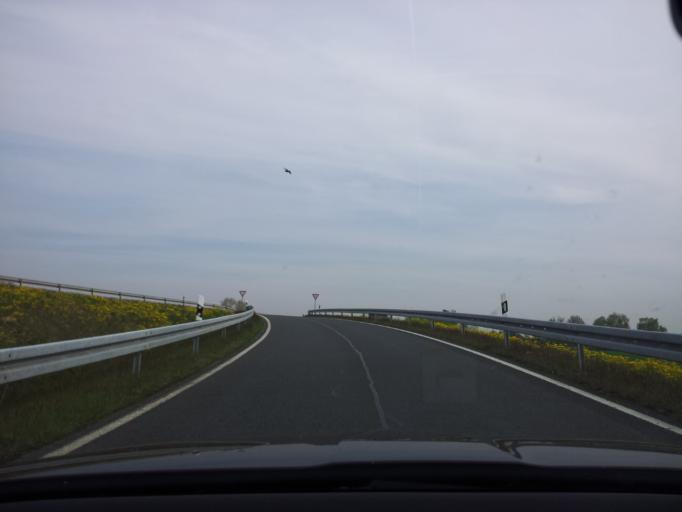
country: DE
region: Brandenburg
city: Luckau
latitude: 51.8539
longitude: 13.6871
